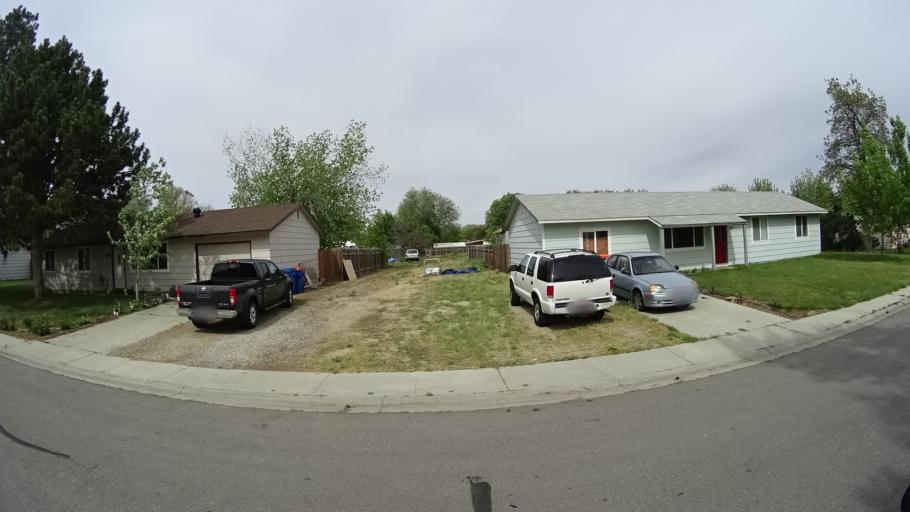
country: US
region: Idaho
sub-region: Ada County
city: Garden City
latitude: 43.5375
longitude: -116.3052
